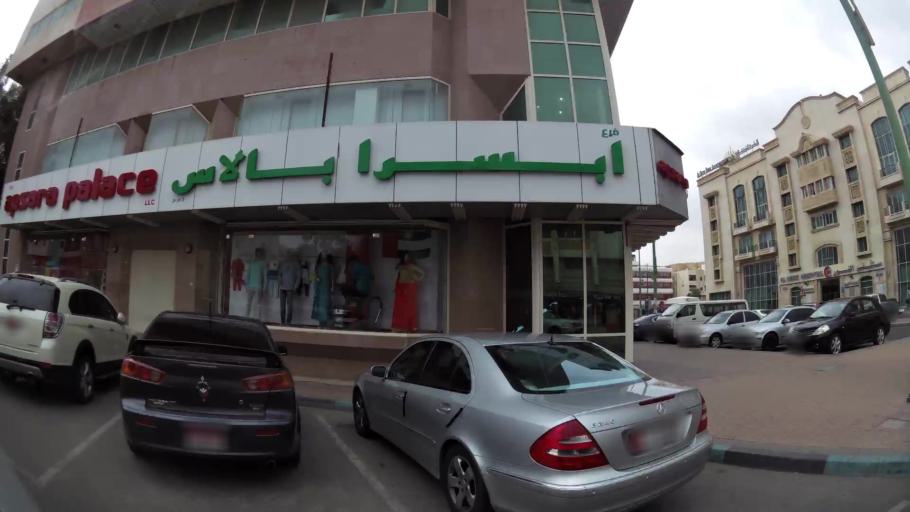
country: AE
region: Abu Dhabi
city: Al Ain
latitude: 24.2229
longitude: 55.7688
